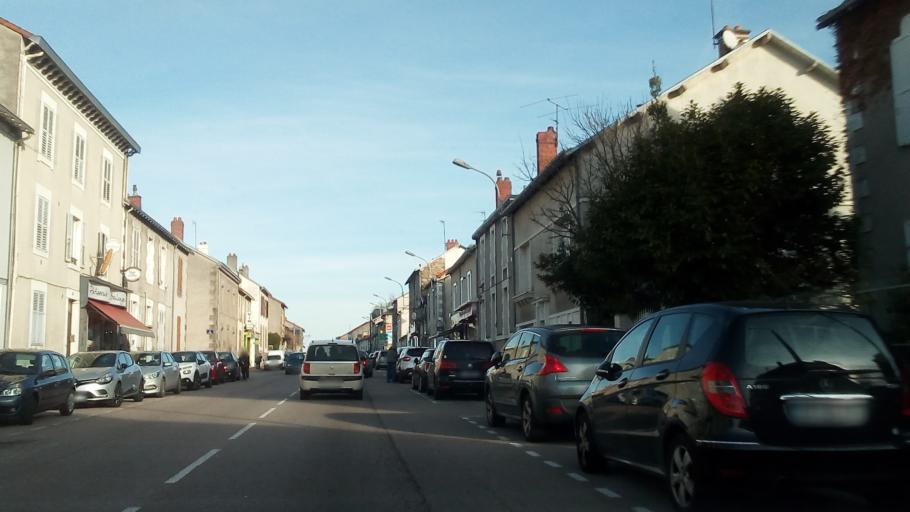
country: FR
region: Limousin
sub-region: Departement de la Haute-Vienne
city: Limoges
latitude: 45.8455
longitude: 1.2456
